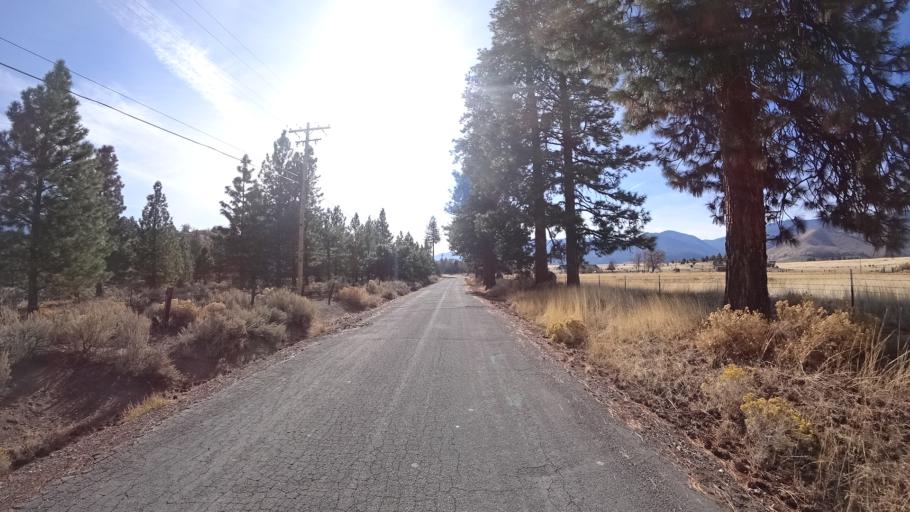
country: US
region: California
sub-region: Siskiyou County
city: Weed
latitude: 41.4848
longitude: -122.4433
